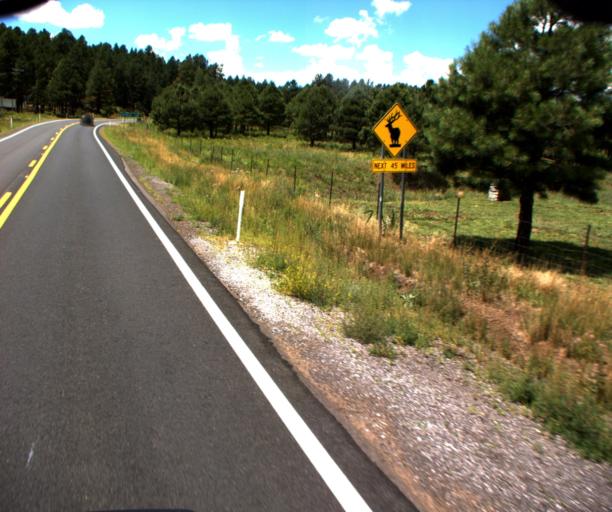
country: US
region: Arizona
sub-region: Coconino County
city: Flagstaff
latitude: 35.2396
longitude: -111.6794
